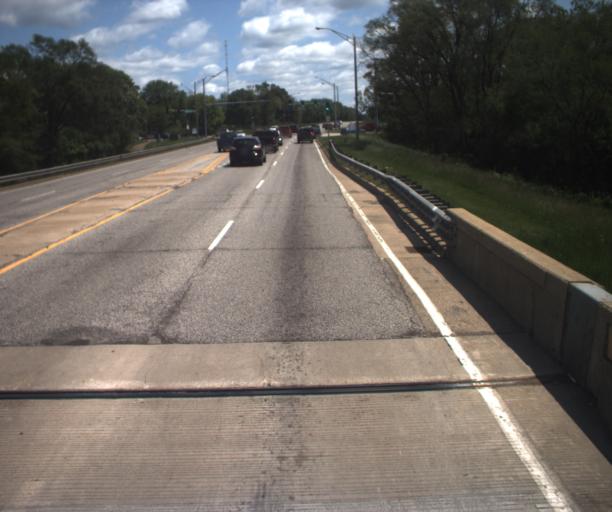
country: US
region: Illinois
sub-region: Kane County
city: Batavia
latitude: 41.8661
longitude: -88.3078
